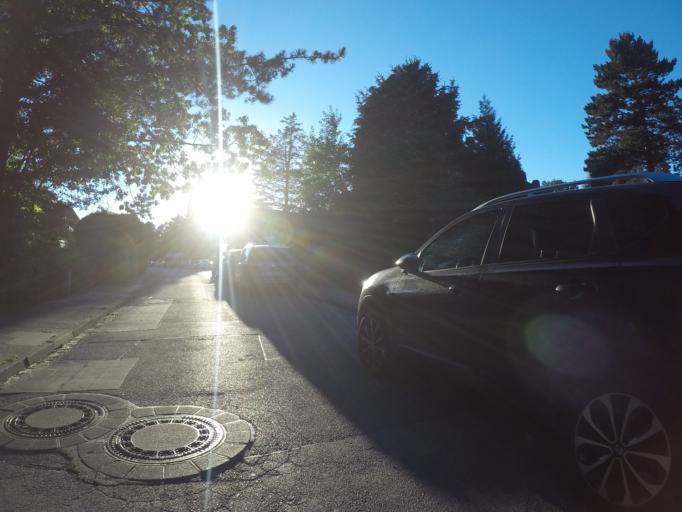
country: DE
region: Hamburg
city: Fuhlsbuettel
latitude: 53.6473
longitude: 10.0231
